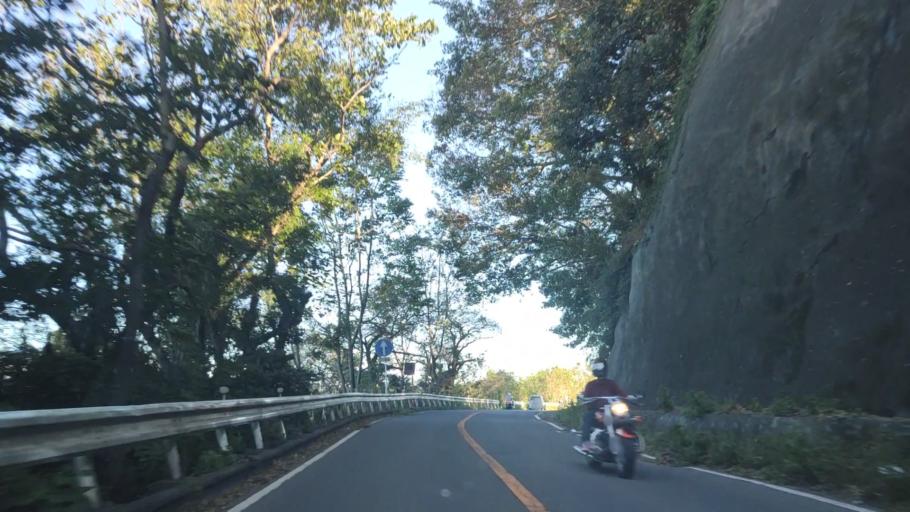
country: JP
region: Kanagawa
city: Zama
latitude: 35.5306
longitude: 139.3445
